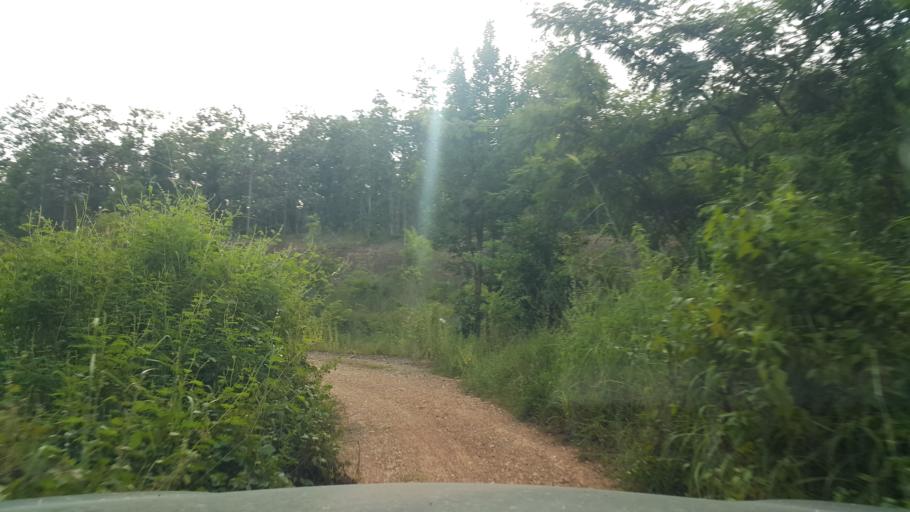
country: TH
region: Chiang Mai
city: San Sai
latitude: 18.9254
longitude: 99.0750
